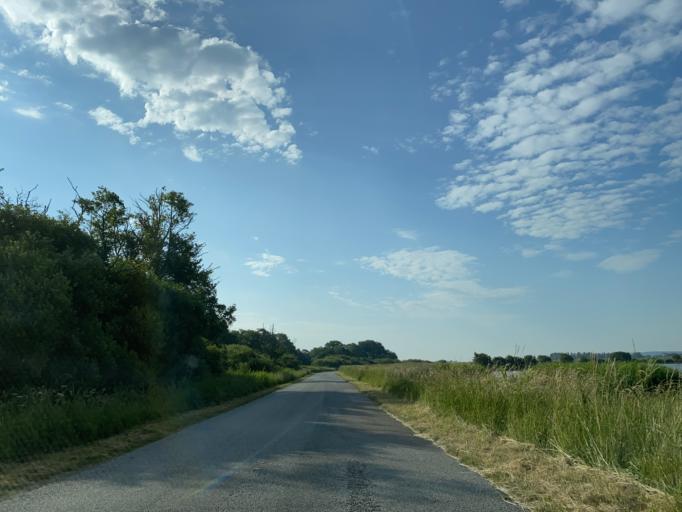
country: DK
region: South Denmark
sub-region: Haderslev Kommune
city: Haderslev
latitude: 55.1703
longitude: 9.4884
